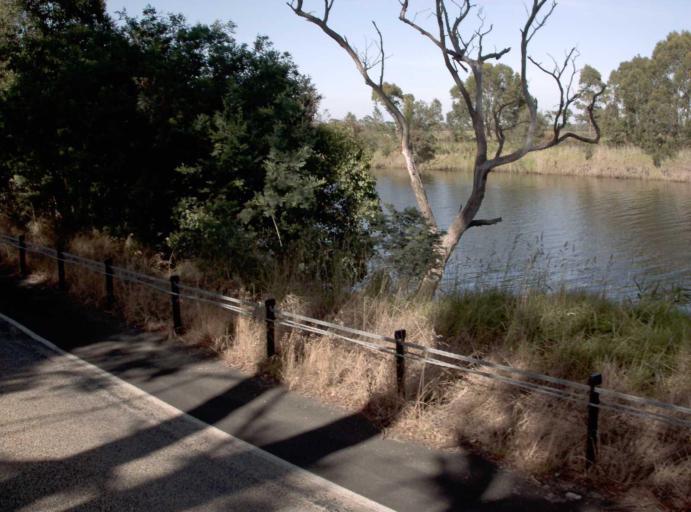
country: AU
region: Victoria
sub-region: East Gippsland
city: Lakes Entrance
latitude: -37.8390
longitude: 147.8605
